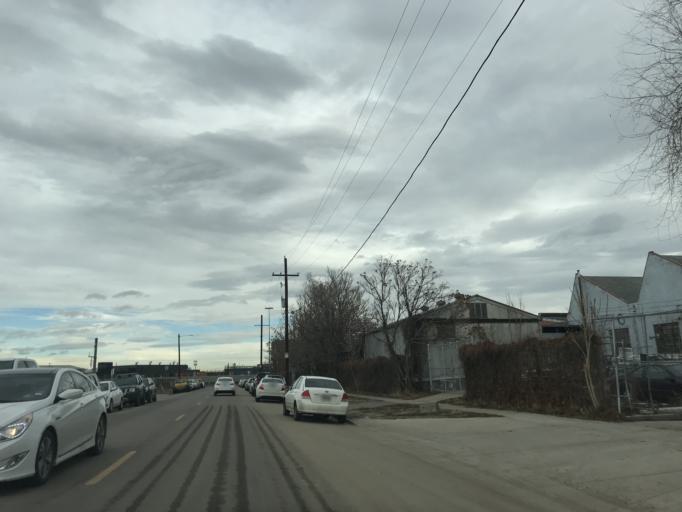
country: US
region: Colorado
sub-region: Denver County
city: Denver
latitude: 39.7715
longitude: -104.9684
